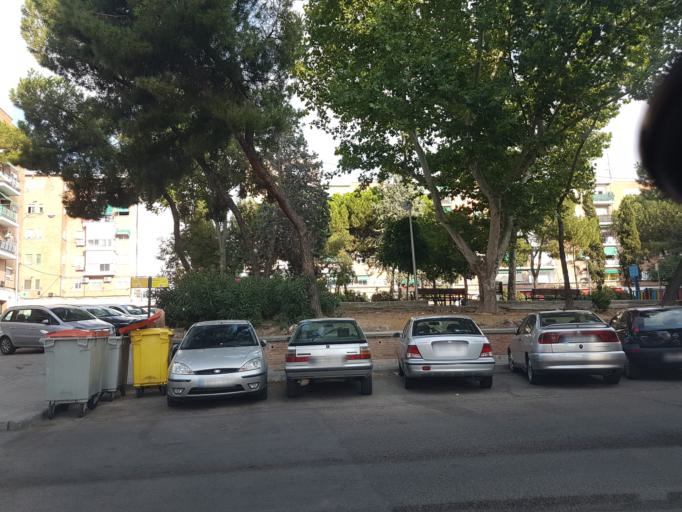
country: ES
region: Madrid
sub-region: Provincia de Madrid
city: Puente de Vallecas
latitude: 40.4041
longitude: -3.6609
